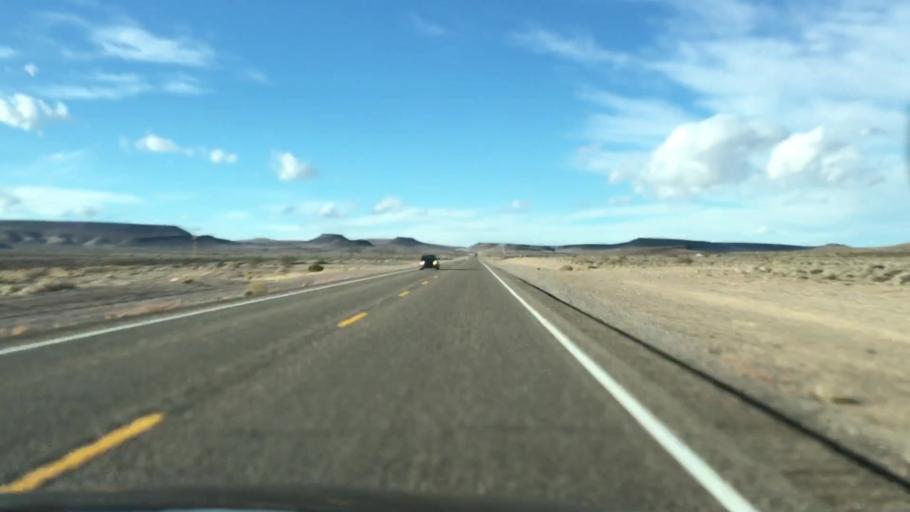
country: US
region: Nevada
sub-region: Esmeralda County
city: Goldfield
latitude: 37.3556
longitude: -117.1109
